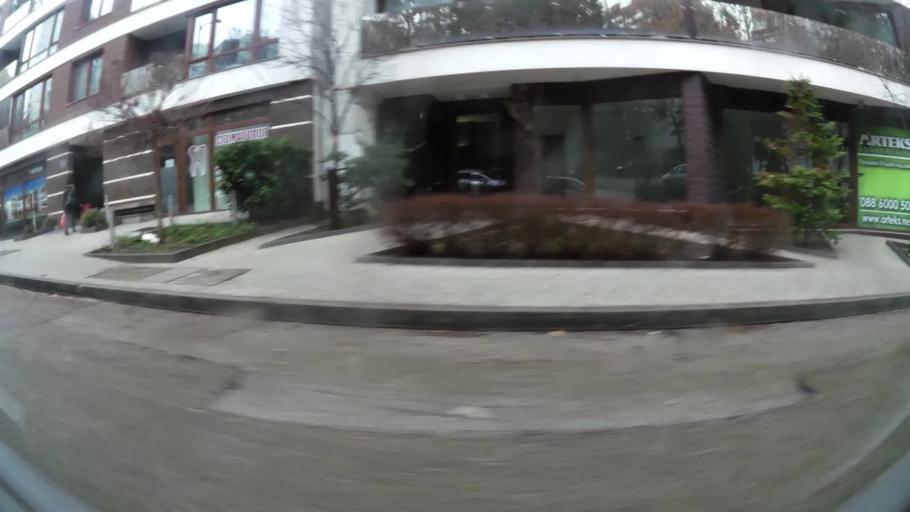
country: BG
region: Sofia-Capital
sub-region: Stolichna Obshtina
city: Sofia
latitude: 42.6384
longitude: 23.3662
